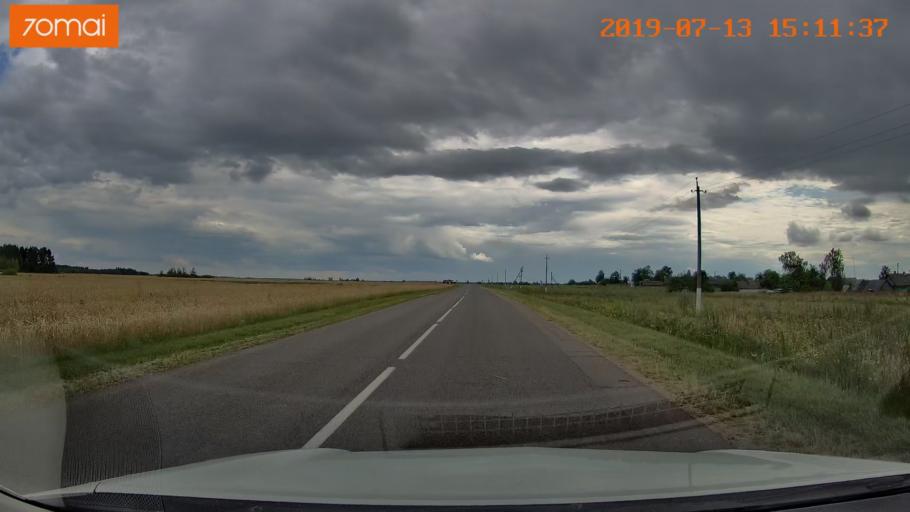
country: BY
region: Mogilev
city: Hlusha
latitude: 53.1591
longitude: 28.7866
